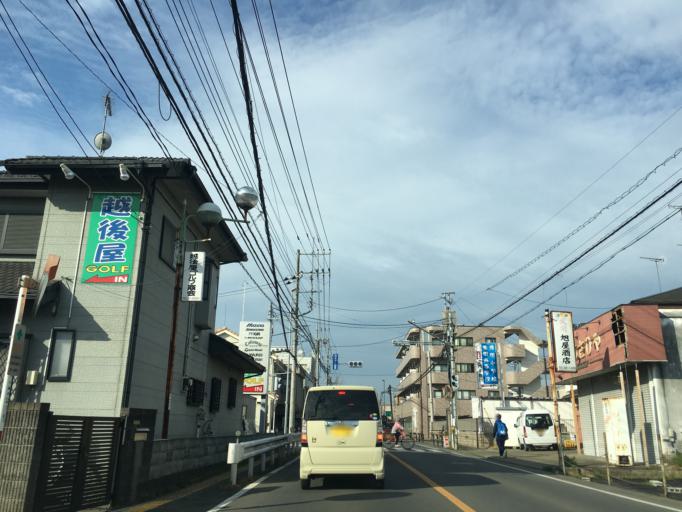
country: JP
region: Saitama
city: Sakado
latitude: 35.9073
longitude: 139.4074
